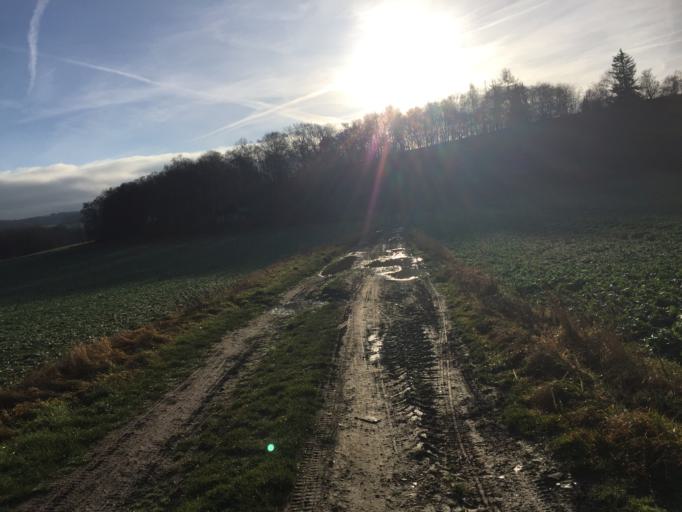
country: DE
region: Thuringia
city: Ranis
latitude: 50.6763
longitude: 11.5805
